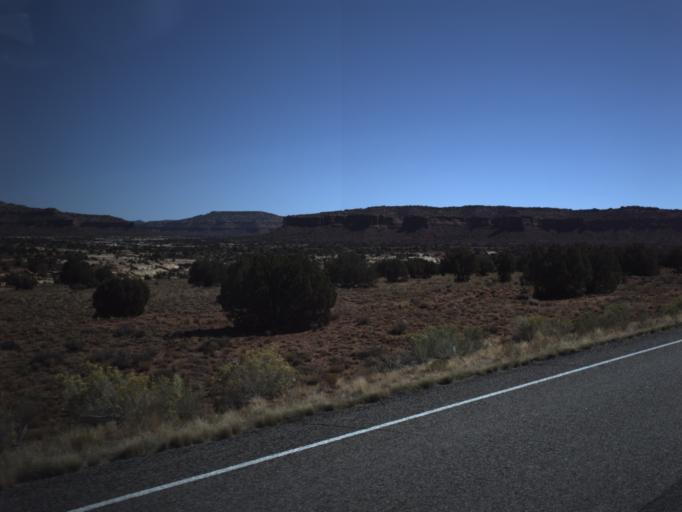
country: US
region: Utah
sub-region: San Juan County
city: Blanding
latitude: 37.7053
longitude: -110.2400
